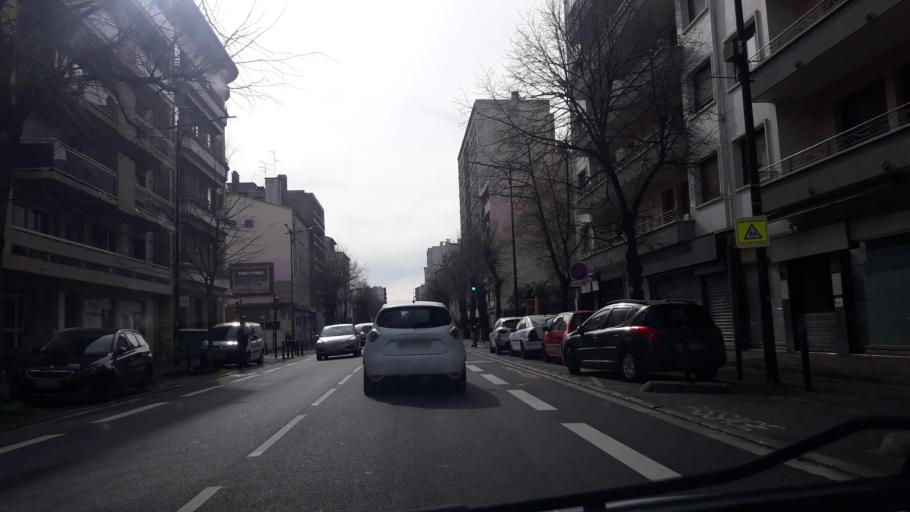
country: FR
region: Midi-Pyrenees
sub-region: Departement de la Haute-Garonne
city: Toulouse
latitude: 43.5833
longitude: 1.4268
